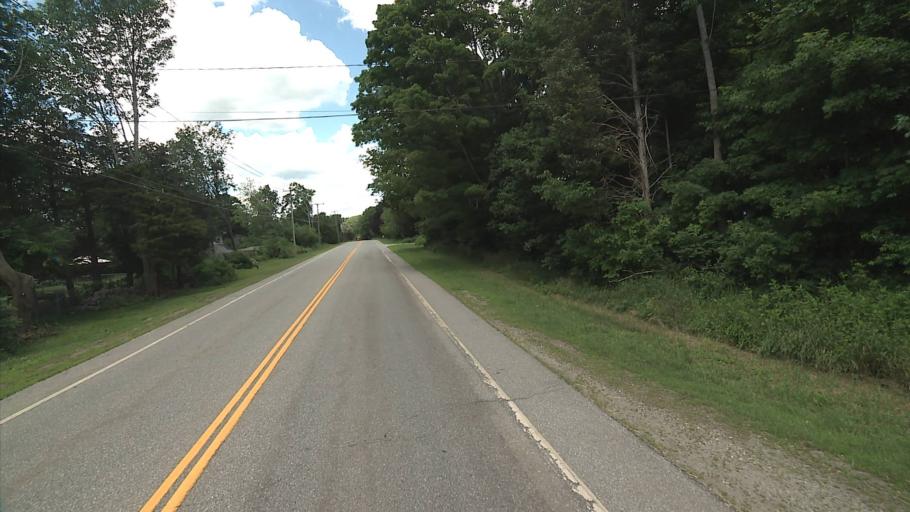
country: US
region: Connecticut
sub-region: New London County
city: Pawcatuck
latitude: 41.4223
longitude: -71.8807
